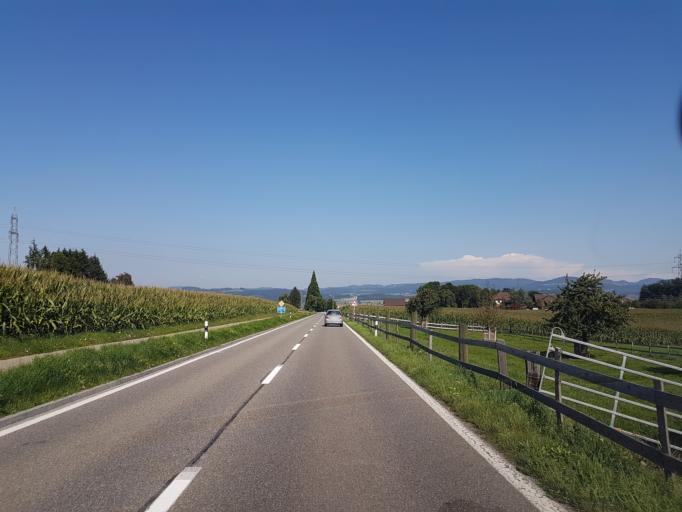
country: CH
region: Aargau
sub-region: Bezirk Muri
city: Muri
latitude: 47.2770
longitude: 8.3516
